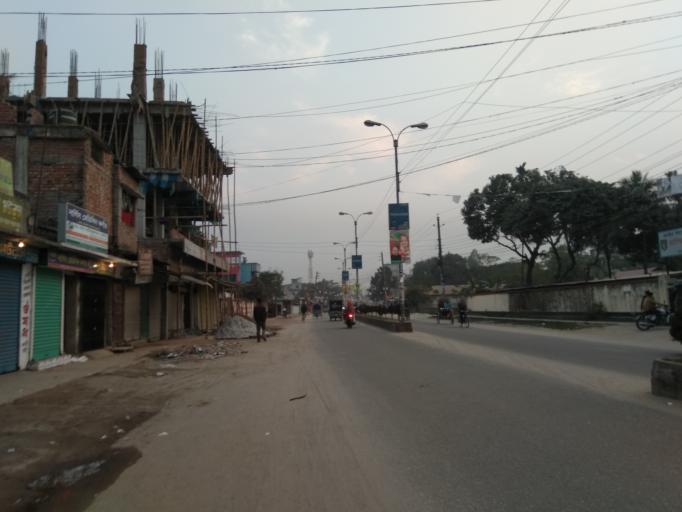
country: BD
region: Rangpur Division
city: Rangpur
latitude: 25.7394
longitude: 89.2547
